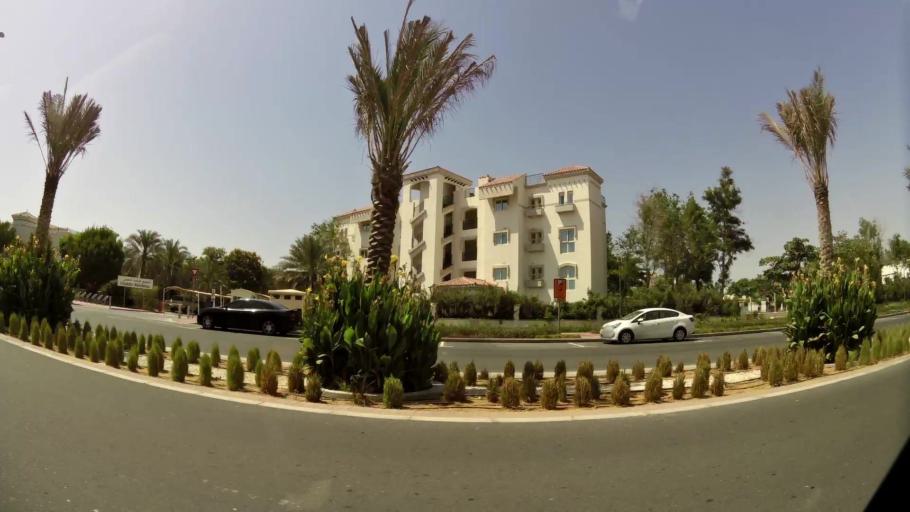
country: AE
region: Dubai
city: Dubai
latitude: 25.1048
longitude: 55.1653
